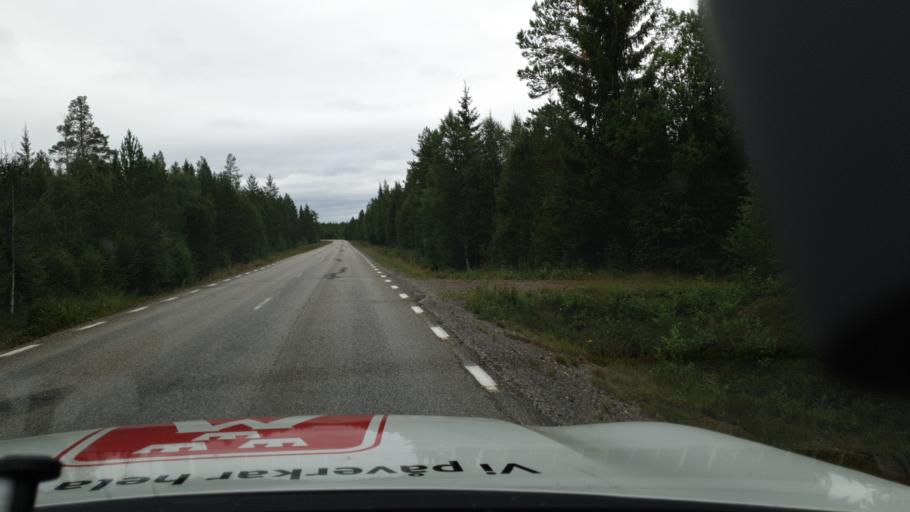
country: SE
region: Vaesterbotten
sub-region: Umea Kommun
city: Saevar
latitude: 64.0625
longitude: 20.4933
